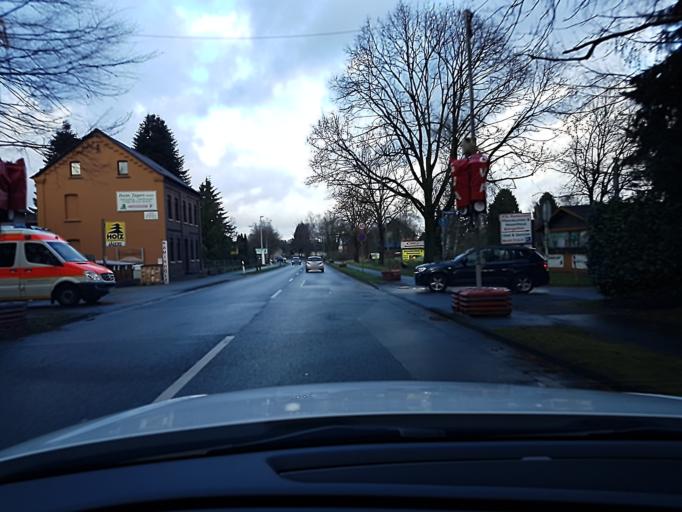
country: DE
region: North Rhine-Westphalia
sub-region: Regierungsbezirk Dusseldorf
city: Muelheim (Ruhr)
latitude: 51.3845
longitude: 6.8655
